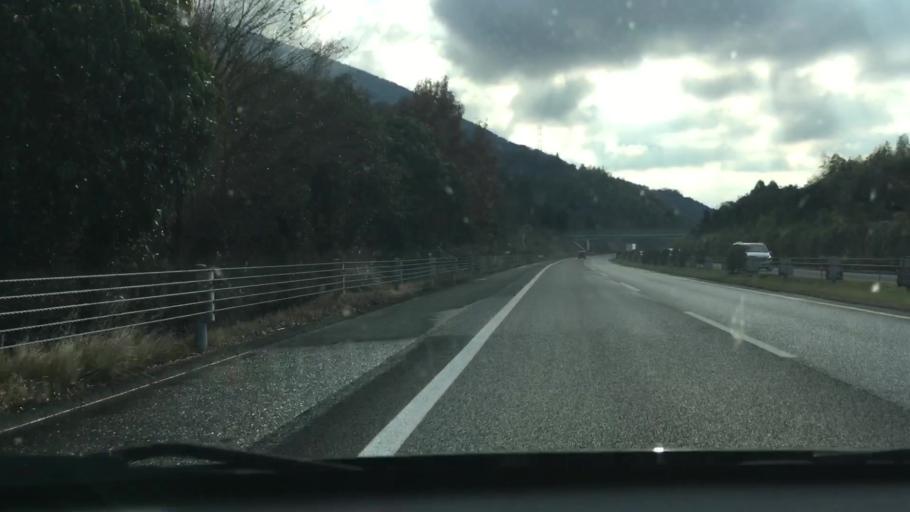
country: JP
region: Kumamoto
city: Yatsushiro
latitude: 32.5352
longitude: 130.6721
